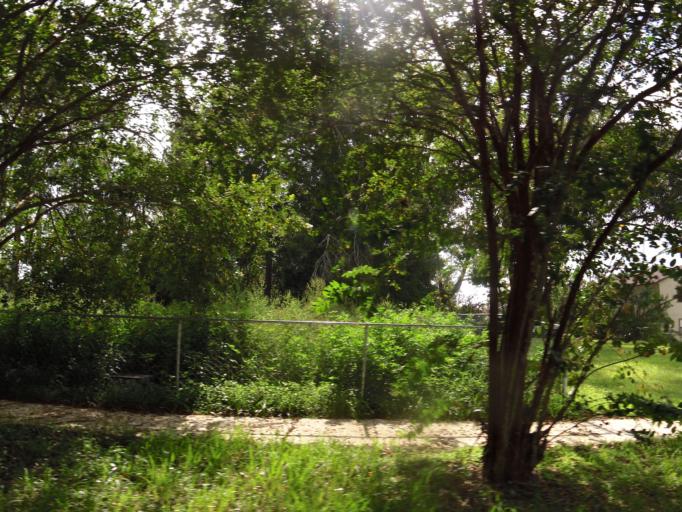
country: US
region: Florida
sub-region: Duval County
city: Jacksonville
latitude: 30.3645
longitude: -81.6883
